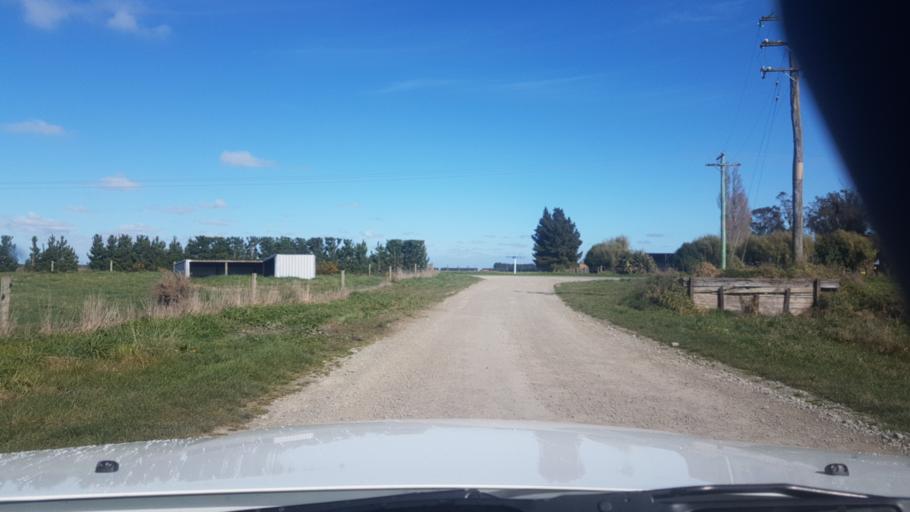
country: NZ
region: Canterbury
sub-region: Ashburton District
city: Tinwald
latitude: -44.1025
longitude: 171.4498
